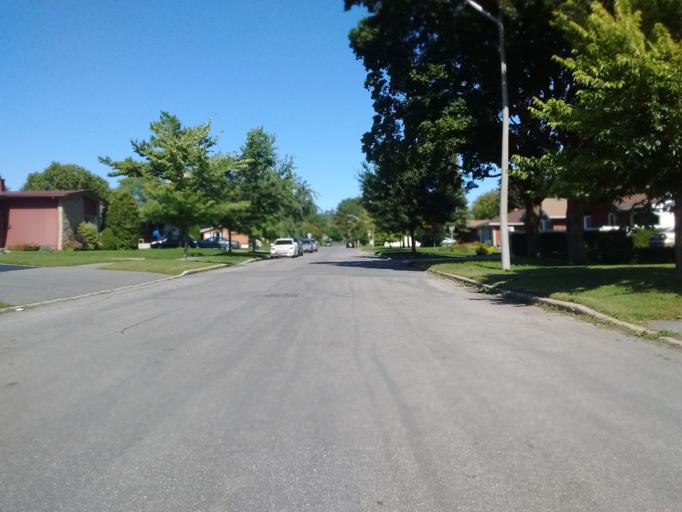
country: CA
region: Ontario
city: Ottawa
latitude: 45.4373
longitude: -75.6412
